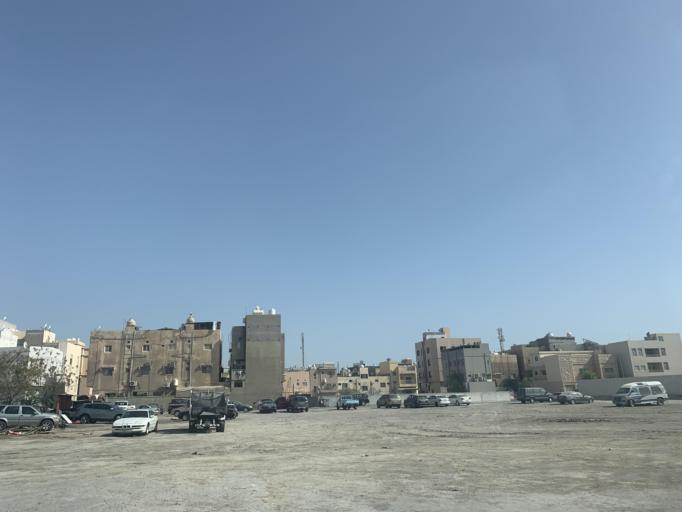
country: BH
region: Manama
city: Jidd Hafs
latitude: 26.2090
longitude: 50.5601
